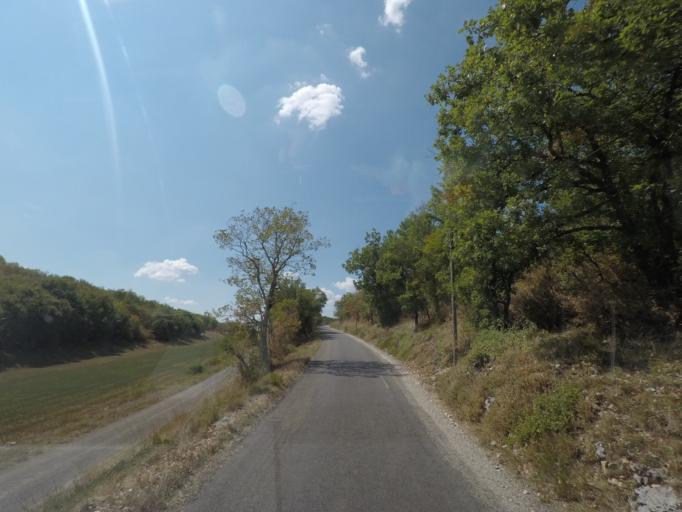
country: FR
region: Midi-Pyrenees
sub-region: Departement du Lot
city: Lalbenque
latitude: 44.5162
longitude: 1.6356
